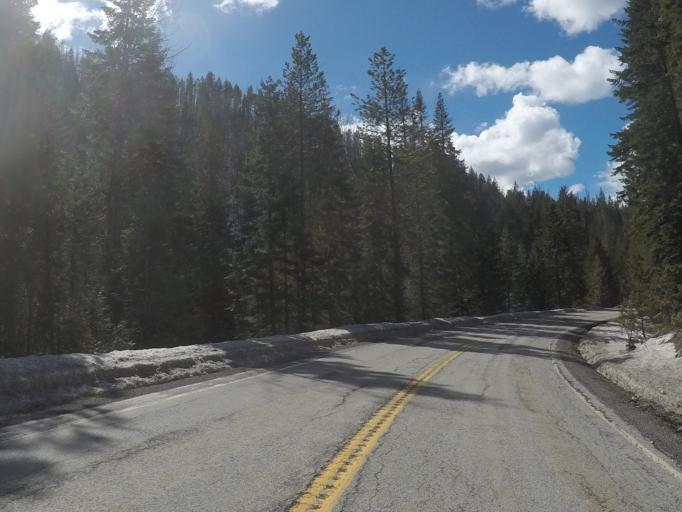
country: US
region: Montana
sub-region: Mineral County
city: Superior
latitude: 46.4767
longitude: -114.8747
